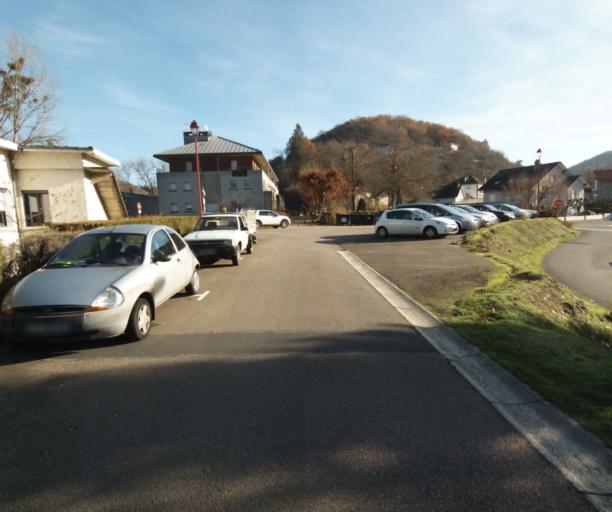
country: FR
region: Limousin
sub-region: Departement de la Correze
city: Laguenne
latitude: 45.2449
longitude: 1.7759
